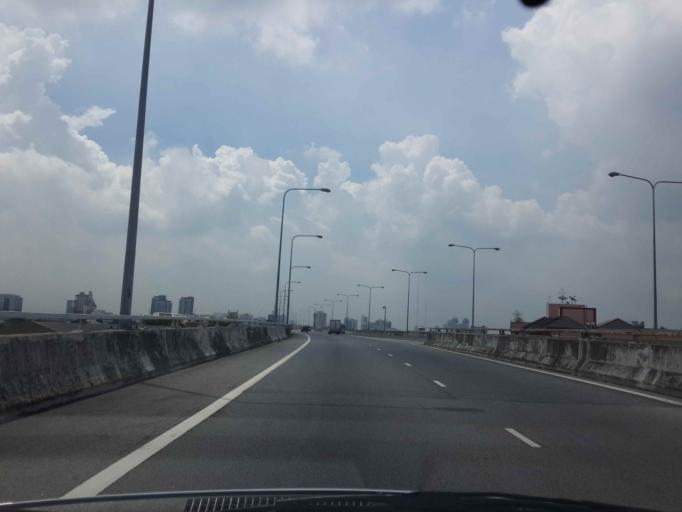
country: TH
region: Bangkok
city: Phra Khanong
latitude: 13.6967
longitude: 100.5942
